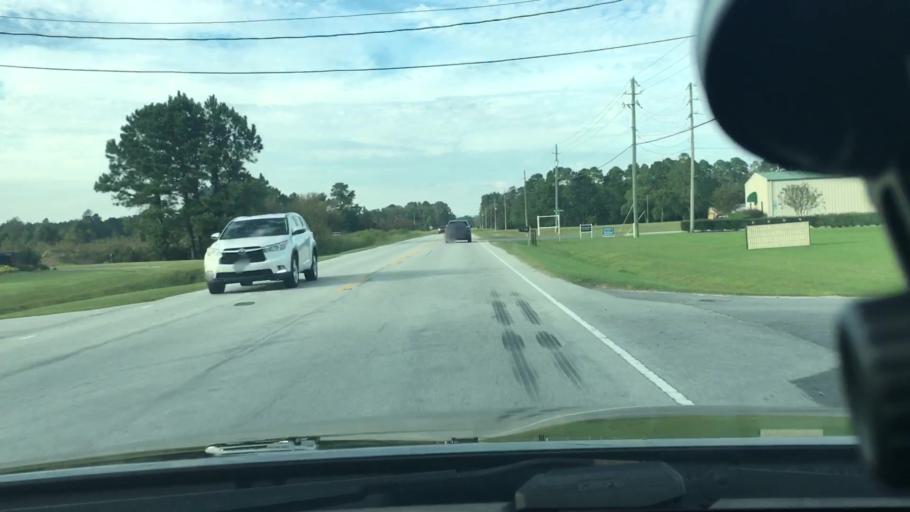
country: US
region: North Carolina
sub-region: Pitt County
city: Windsor
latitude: 35.5177
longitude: -77.3192
